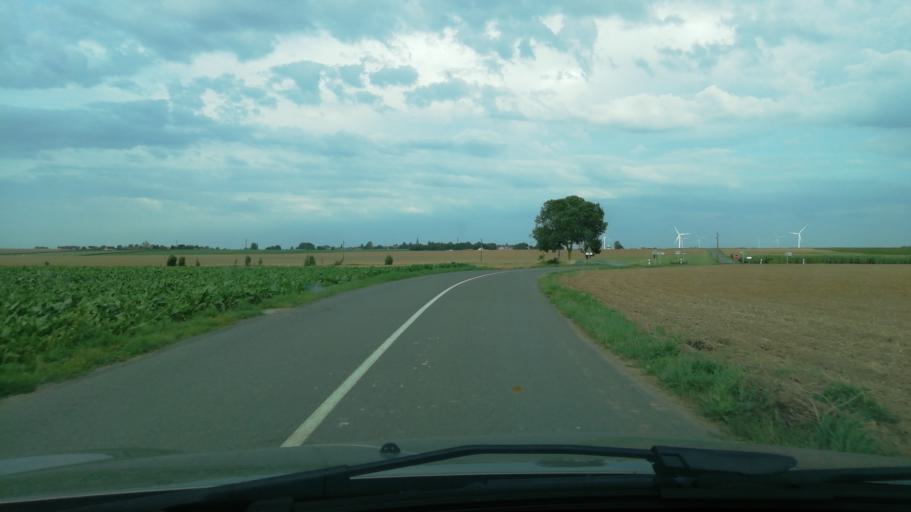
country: FR
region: Nord-Pas-de-Calais
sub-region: Departement du Nord
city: Saint-Hilaire-lez-Cambrai
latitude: 50.1744
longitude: 3.3894
